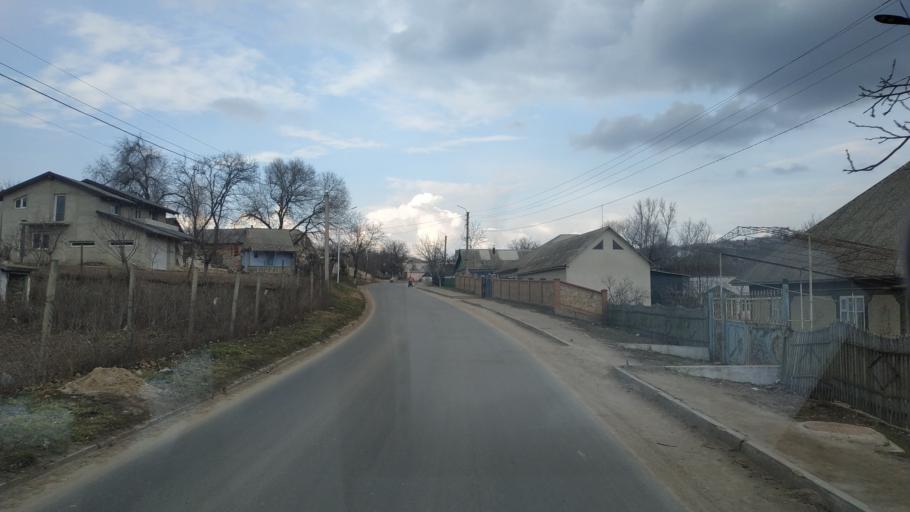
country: MD
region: Anenii Noi
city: Varnita
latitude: 46.8432
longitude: 29.3577
